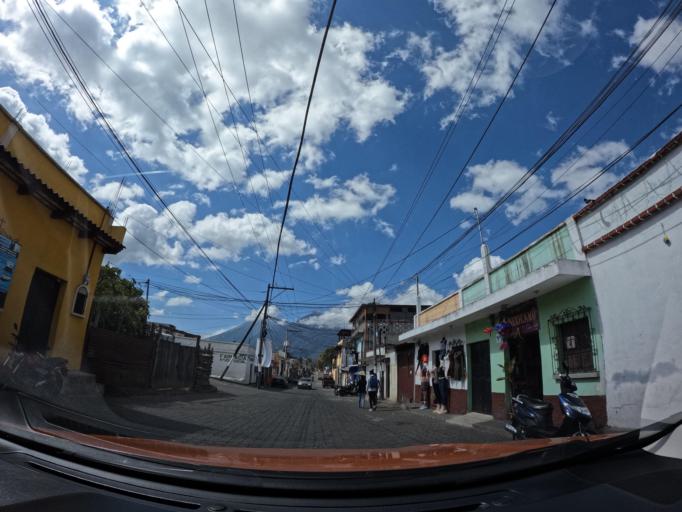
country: GT
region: Sacatepequez
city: Ciudad Vieja
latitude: 14.5253
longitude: -90.7566
